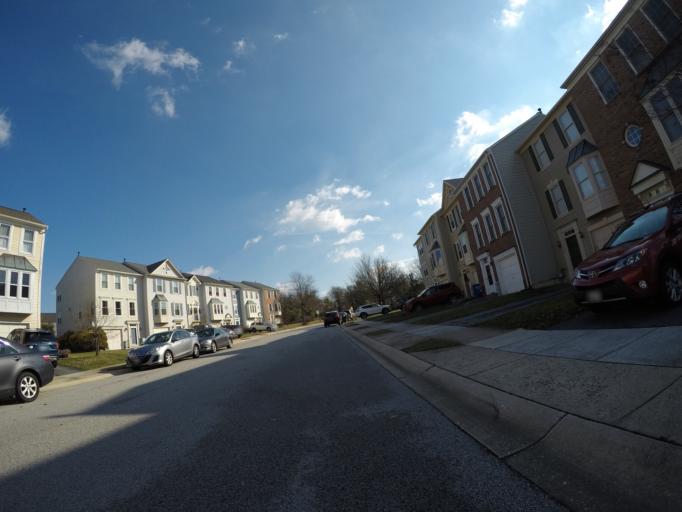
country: US
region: Maryland
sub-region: Howard County
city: Ilchester
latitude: 39.2130
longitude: -76.7863
